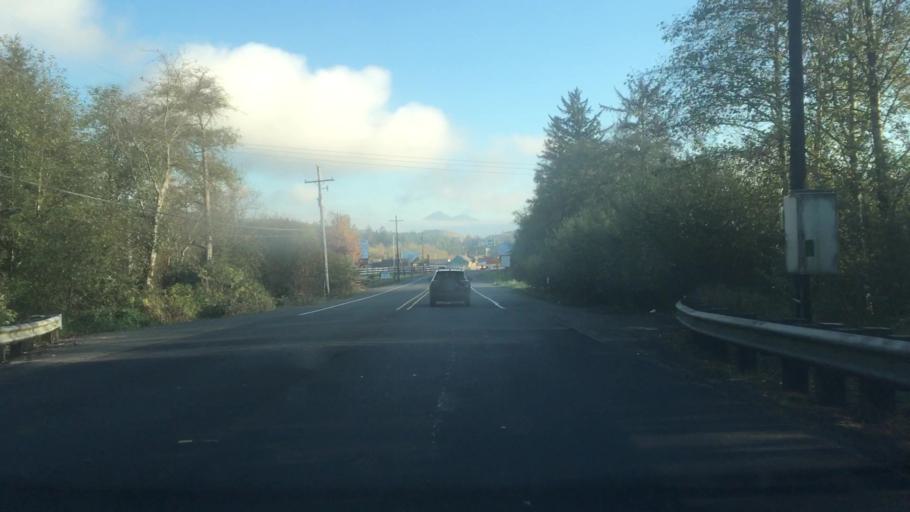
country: US
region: Oregon
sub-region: Clatsop County
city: Seaside
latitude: 45.9746
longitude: -123.9275
